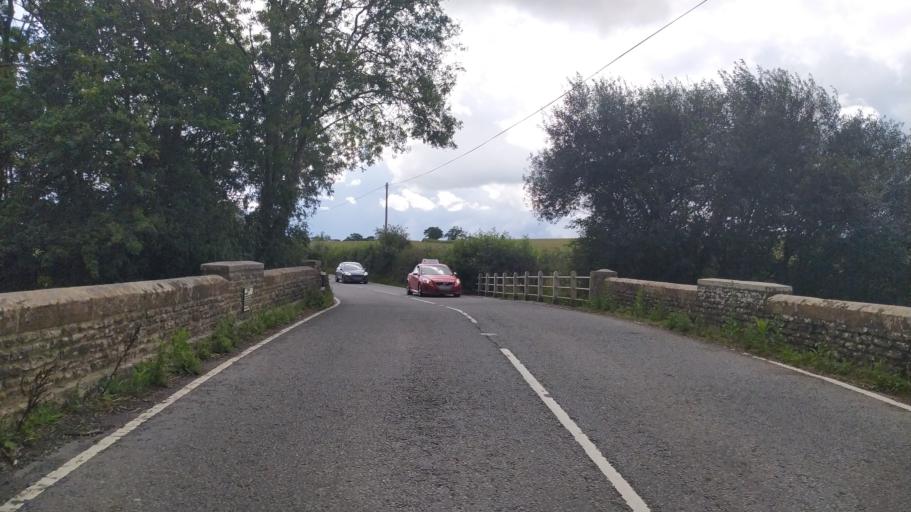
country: GB
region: England
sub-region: Dorset
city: Stalbridge
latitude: 50.9127
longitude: -2.4173
